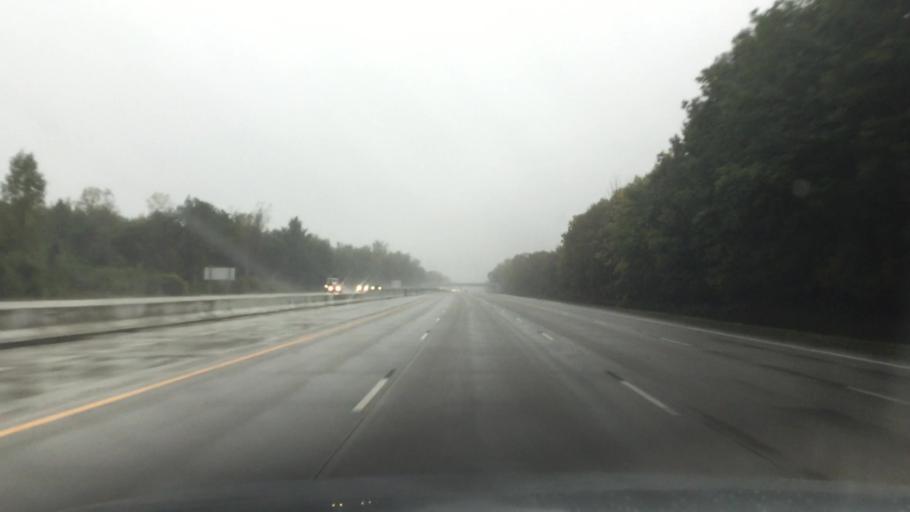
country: US
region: Michigan
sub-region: Saginaw County
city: Bridgeport
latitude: 43.3720
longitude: -83.8713
